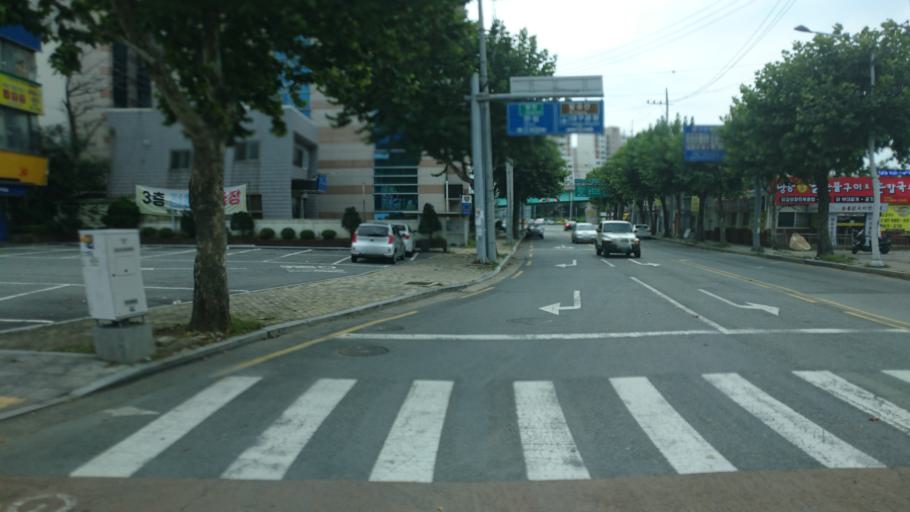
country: KR
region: Gyeongsangbuk-do
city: Gyeongsan-si
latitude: 35.8761
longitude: 128.6814
